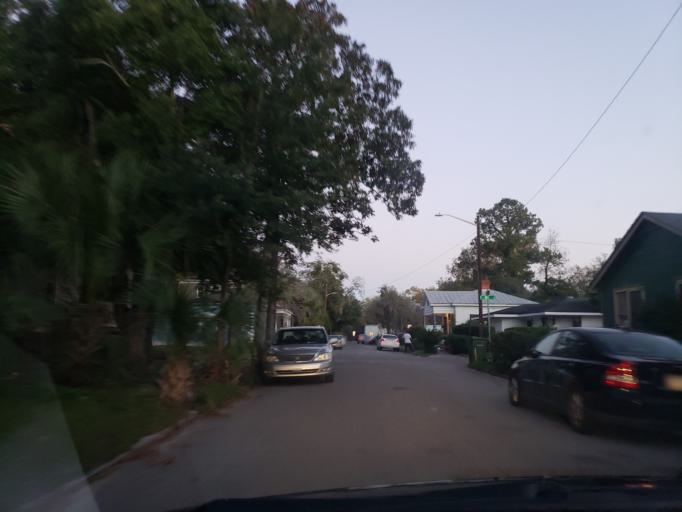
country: US
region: Georgia
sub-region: Chatham County
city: Savannah
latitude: 32.0520
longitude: -81.0856
